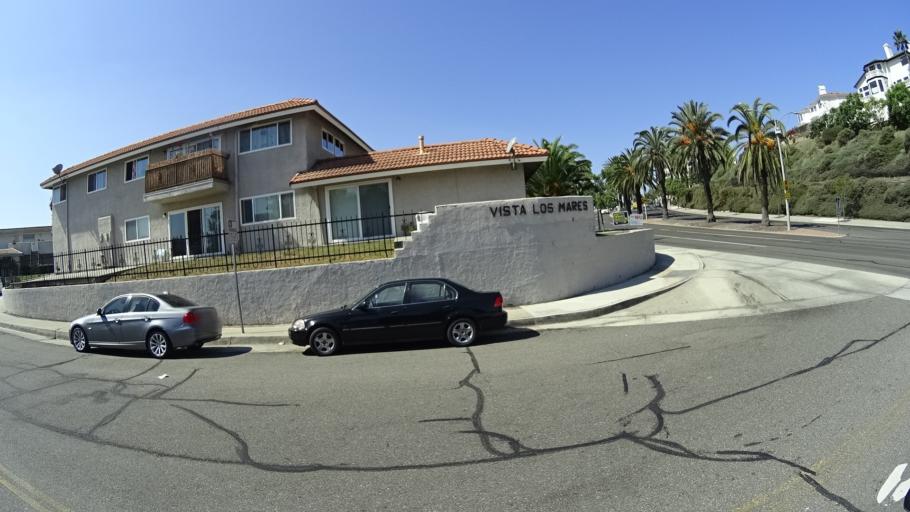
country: US
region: California
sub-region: Orange County
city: San Clemente
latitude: 33.4565
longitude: -117.6451
